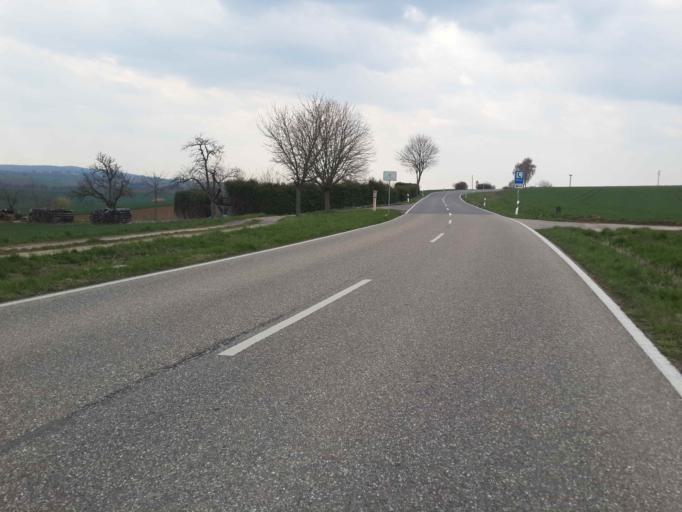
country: DE
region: Baden-Wuerttemberg
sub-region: Regierungsbezirk Stuttgart
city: Eppingen
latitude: 49.1774
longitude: 8.8777
